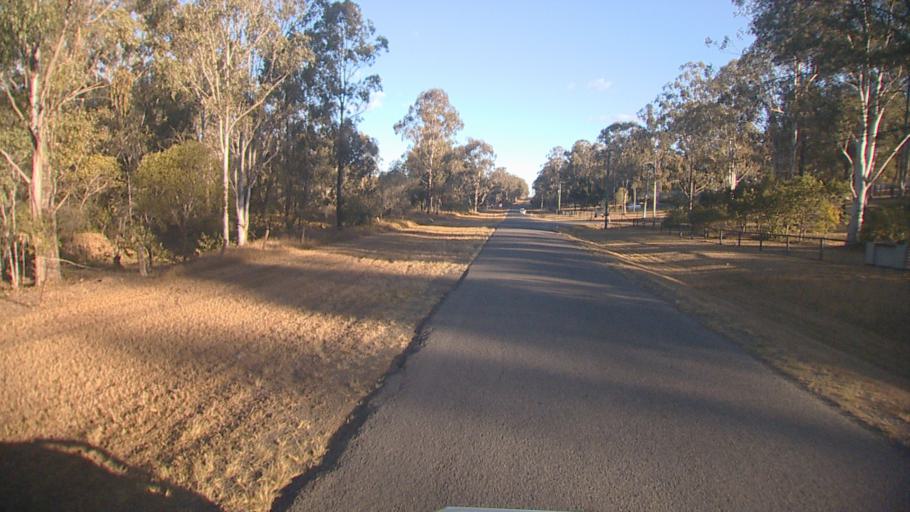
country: AU
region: Queensland
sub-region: Logan
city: Cedar Vale
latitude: -27.8627
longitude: 152.9777
